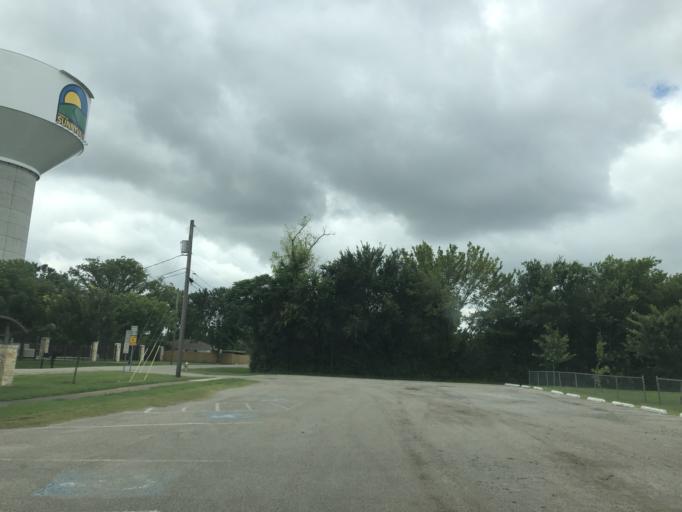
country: US
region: Texas
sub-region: Dallas County
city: Sunnyvale
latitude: 32.8154
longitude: -96.5923
